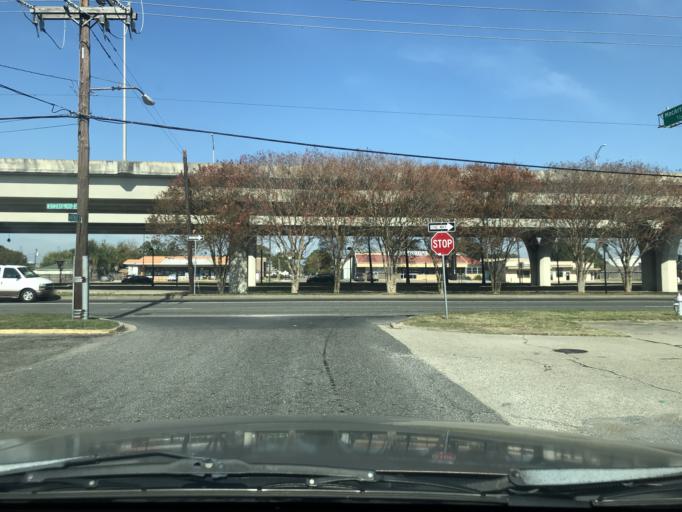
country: US
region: Louisiana
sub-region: Jefferson Parish
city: Marrero
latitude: 29.8942
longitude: -90.0981
